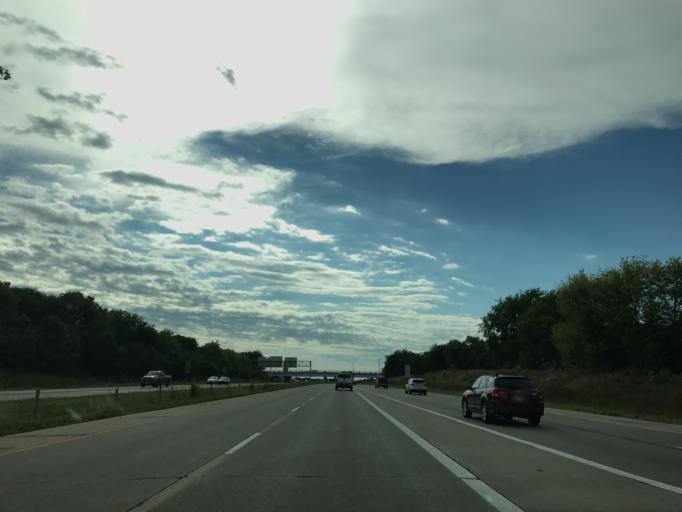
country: US
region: Iowa
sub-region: Polk County
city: Clive
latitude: 41.5923
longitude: -93.7851
